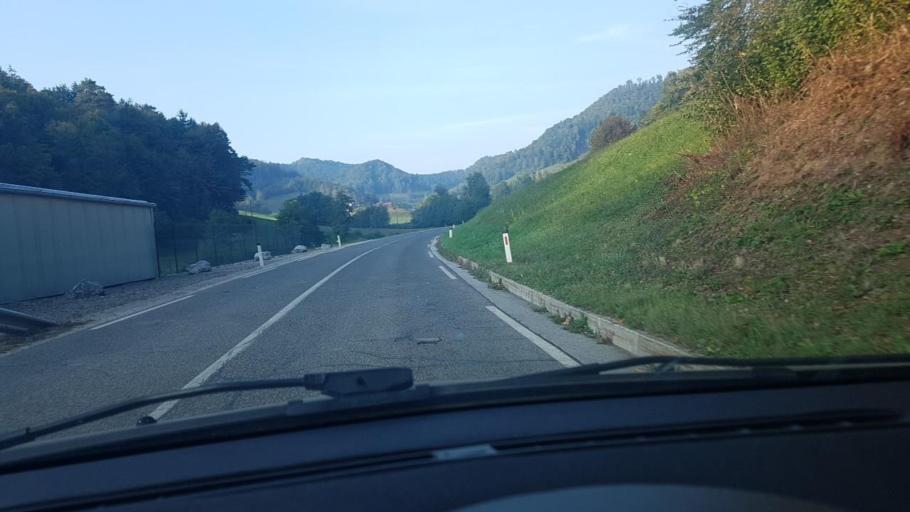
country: SI
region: Rogatec
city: Rogatec
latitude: 46.2481
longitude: 15.7001
